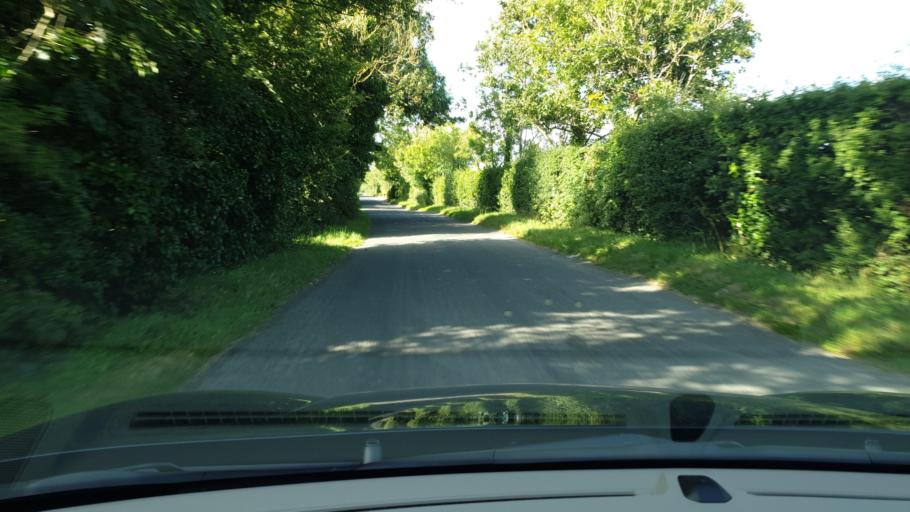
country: IE
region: Leinster
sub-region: An Mhi
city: Ashbourne
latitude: 53.5751
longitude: -6.3503
